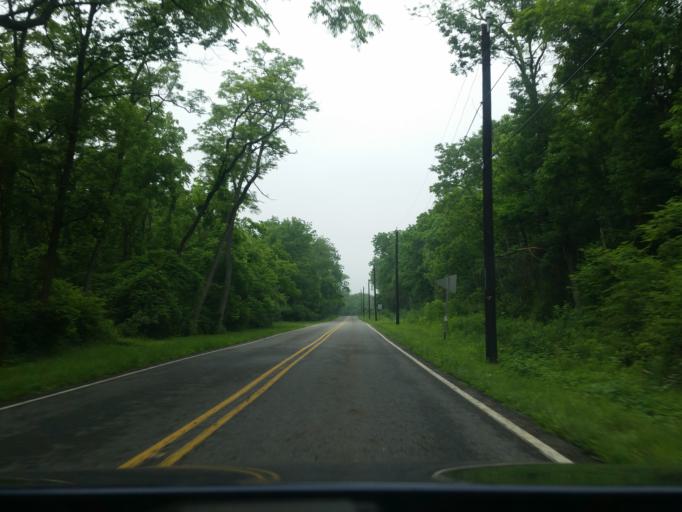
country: US
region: Pennsylvania
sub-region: Lebanon County
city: Jonestown
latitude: 40.4270
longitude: -76.5413
